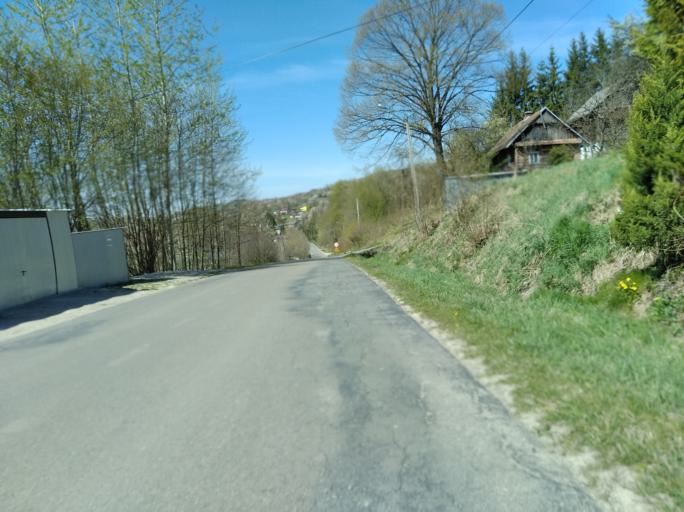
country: PL
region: Subcarpathian Voivodeship
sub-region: Powiat brzozowski
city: Golcowa
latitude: 49.7638
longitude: 22.0541
